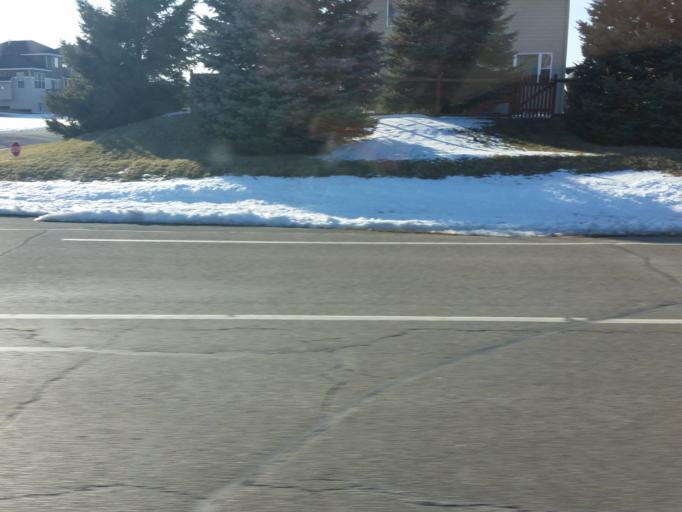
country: US
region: Minnesota
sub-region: Dakota County
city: Lakeville
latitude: 44.6404
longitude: -93.2536
